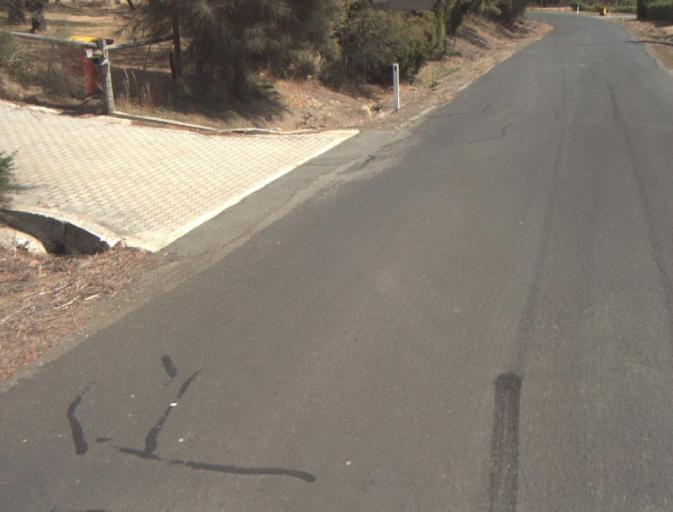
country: AU
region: Tasmania
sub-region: Launceston
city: Newstead
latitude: -41.4448
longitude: 147.2125
